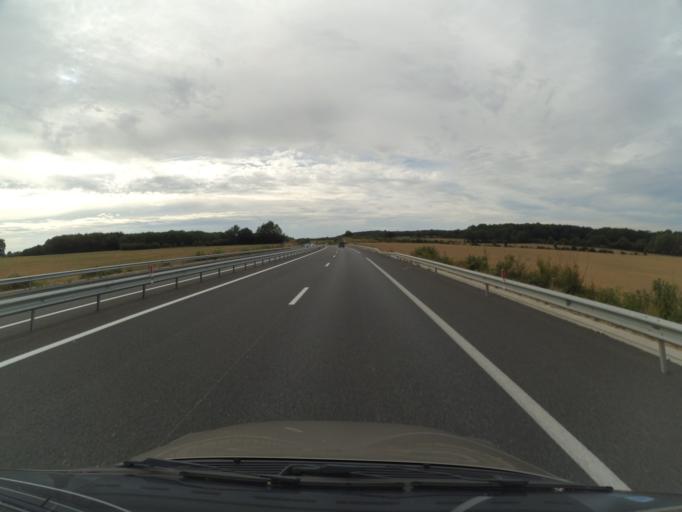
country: FR
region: Poitou-Charentes
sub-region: Departement des Deux-Sevres
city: Nueil-les-Aubiers
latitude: 46.8882
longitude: -0.6054
